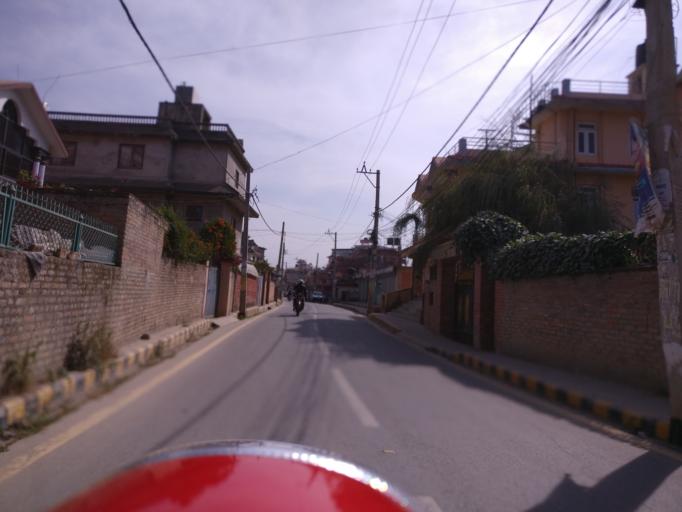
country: NP
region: Central Region
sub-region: Bagmati Zone
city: Patan
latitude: 27.6603
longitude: 85.3162
